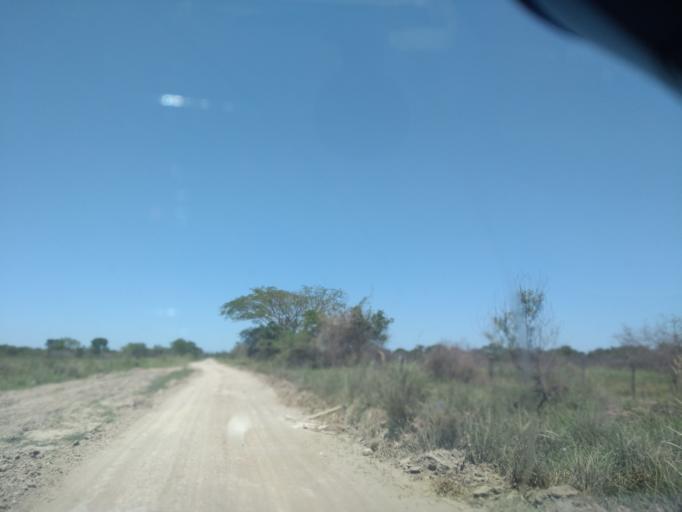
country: AR
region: Chaco
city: Fontana
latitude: -27.3955
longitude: -58.9673
